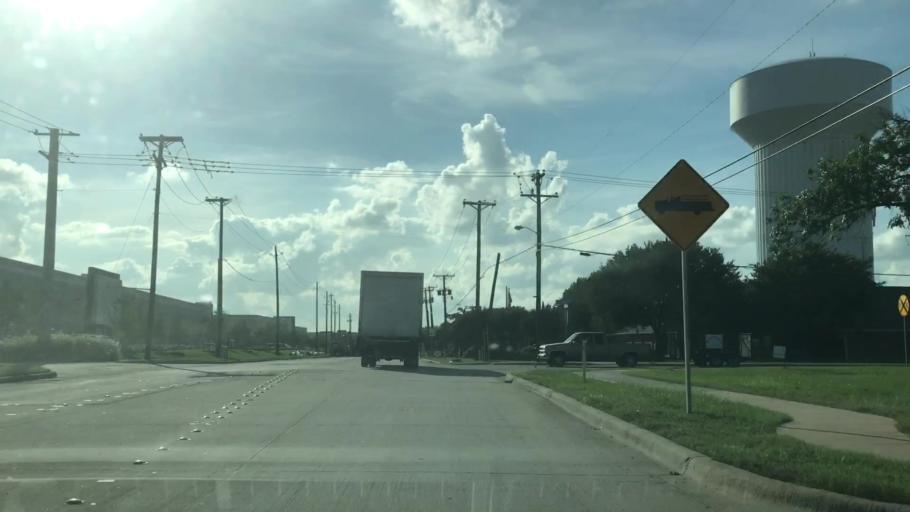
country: US
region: Texas
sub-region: Dallas County
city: Coppell
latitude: 32.9488
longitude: -97.0048
